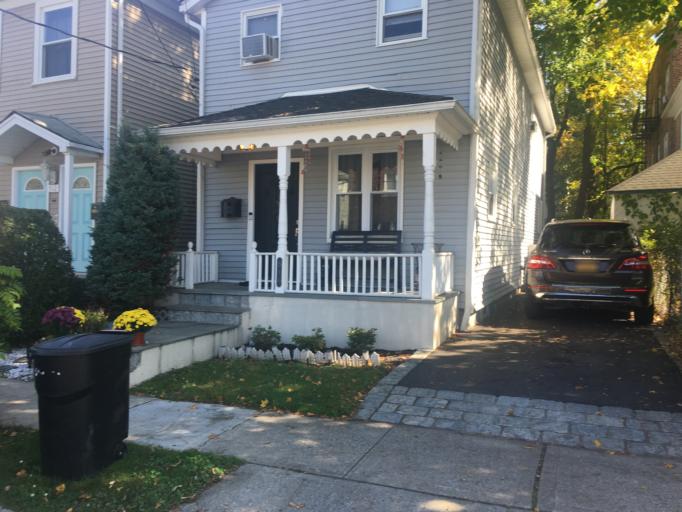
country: US
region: New York
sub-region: Westchester County
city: Pelham
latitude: 40.9185
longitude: -73.8048
